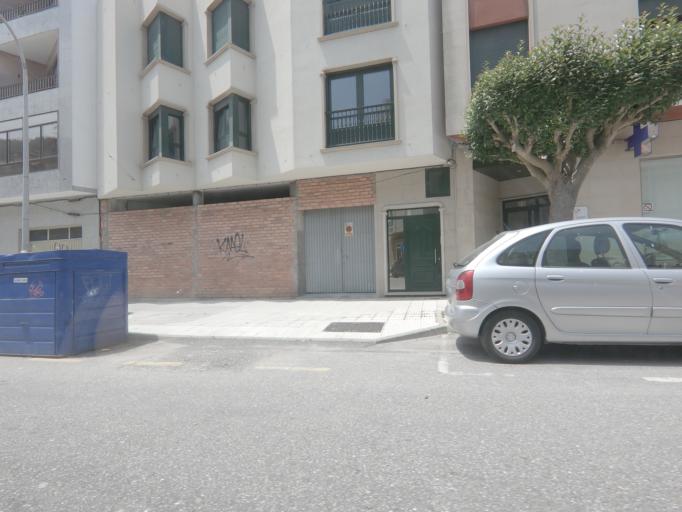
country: ES
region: Galicia
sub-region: Provincia de Pontevedra
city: A Guarda
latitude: 41.9011
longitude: -8.8703
